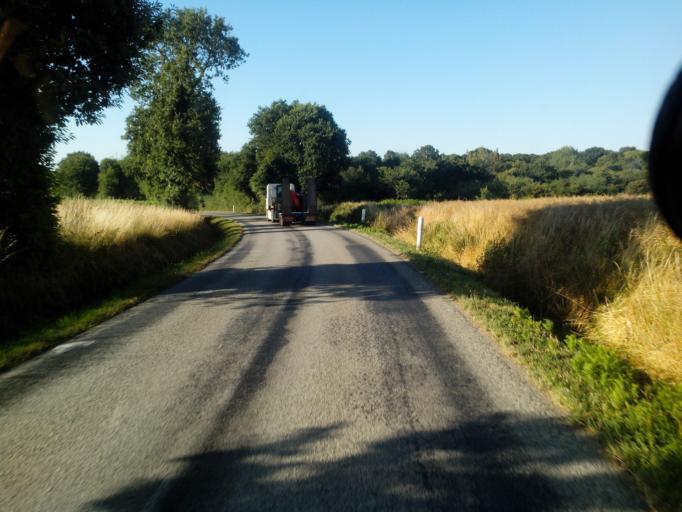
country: FR
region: Brittany
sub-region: Departement du Morbihan
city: Loyat
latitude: 48.0085
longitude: -2.3939
